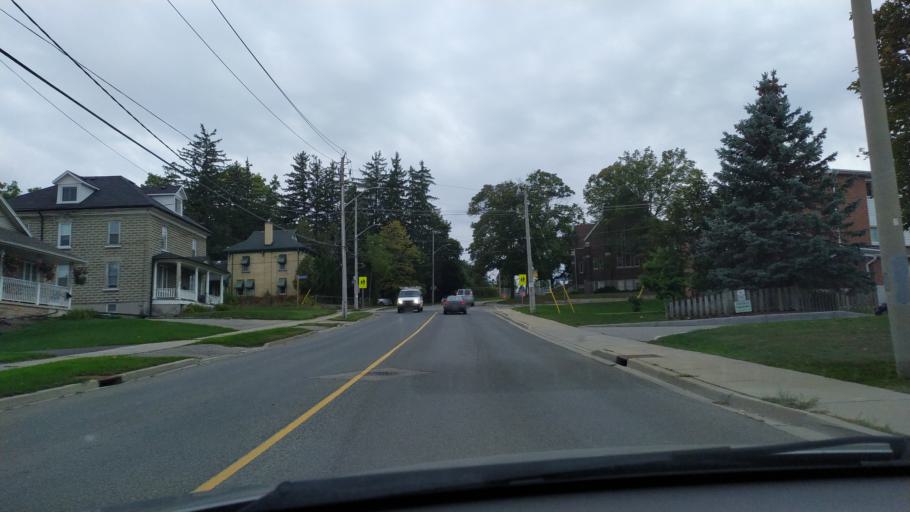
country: CA
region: Ontario
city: Waterloo
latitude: 43.4826
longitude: -80.4838
